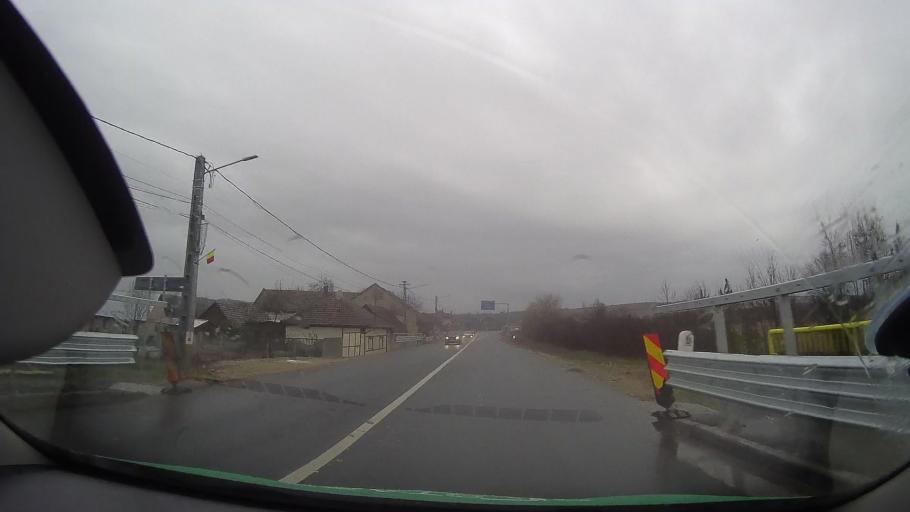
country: RO
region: Bihor
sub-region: Comuna Pocola
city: Pocola
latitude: 46.6974
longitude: 22.2887
